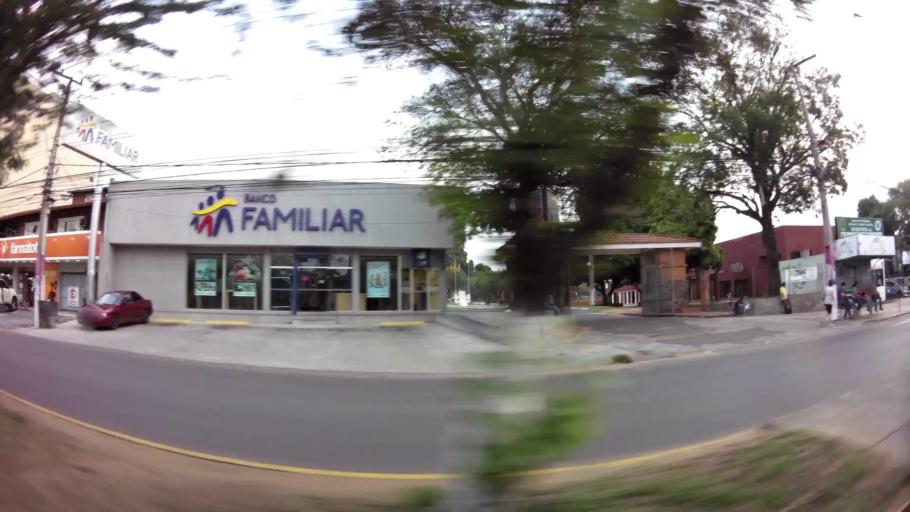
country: PY
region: Central
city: Lambare
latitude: -25.3429
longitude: -57.6224
